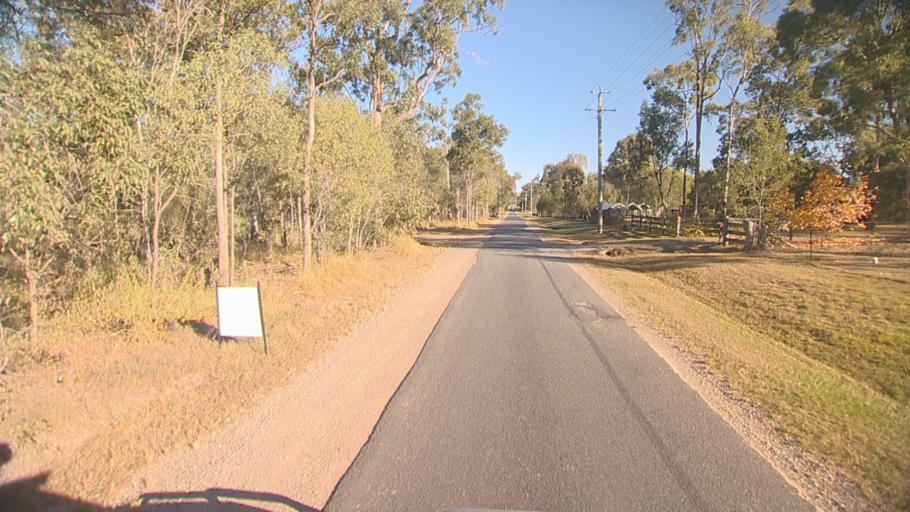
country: AU
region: Queensland
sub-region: Logan
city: North Maclean
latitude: -27.7833
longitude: 153.0395
